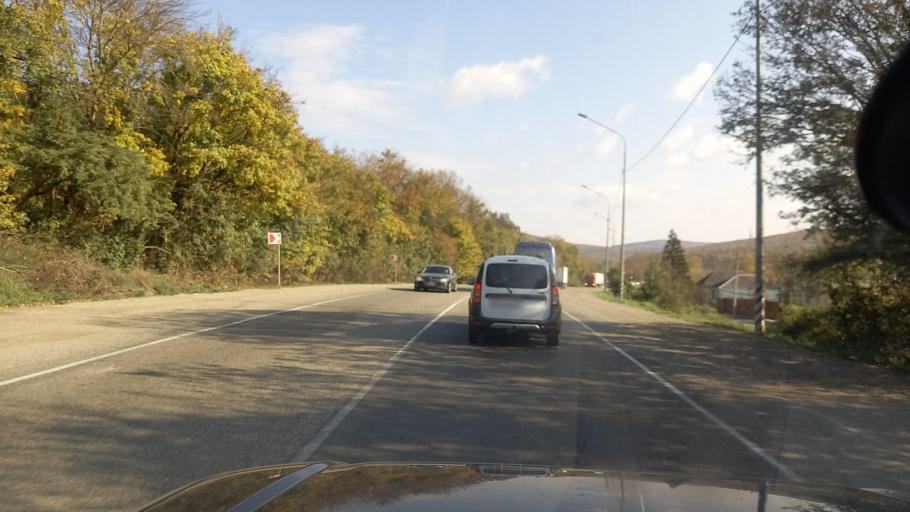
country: RU
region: Krasnodarskiy
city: Verkhnebakanskiy
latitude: 44.8633
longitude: 37.7389
